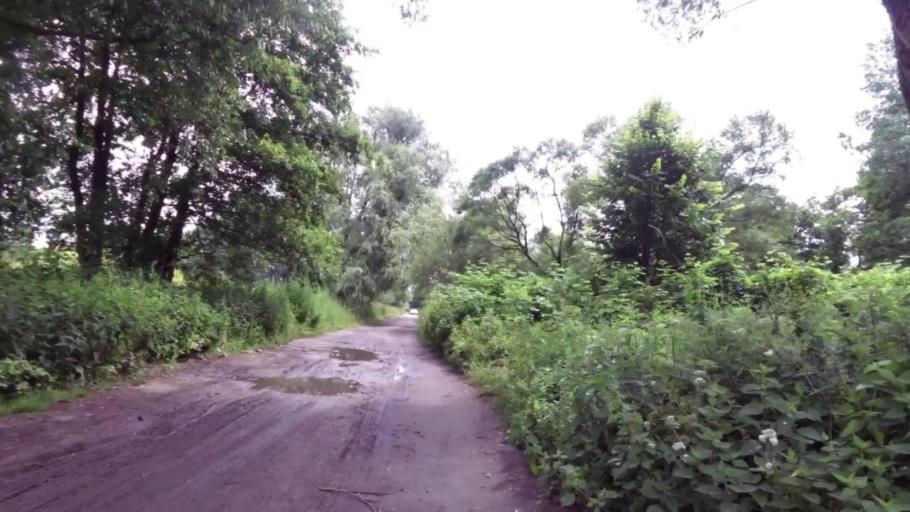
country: PL
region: West Pomeranian Voivodeship
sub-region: Szczecin
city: Szczecin
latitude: 53.4052
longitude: 14.6710
